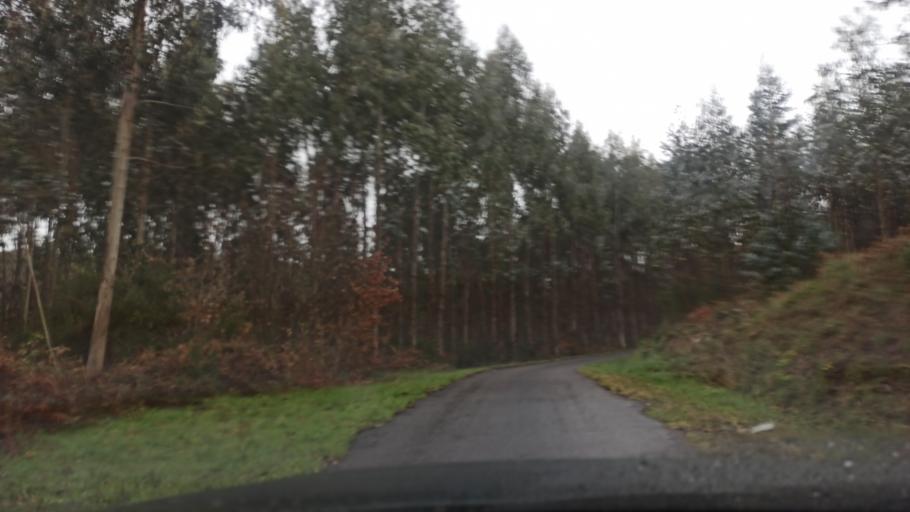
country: ES
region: Galicia
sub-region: Provincia da Coruna
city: Cesuras
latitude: 43.1778
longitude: -8.1570
